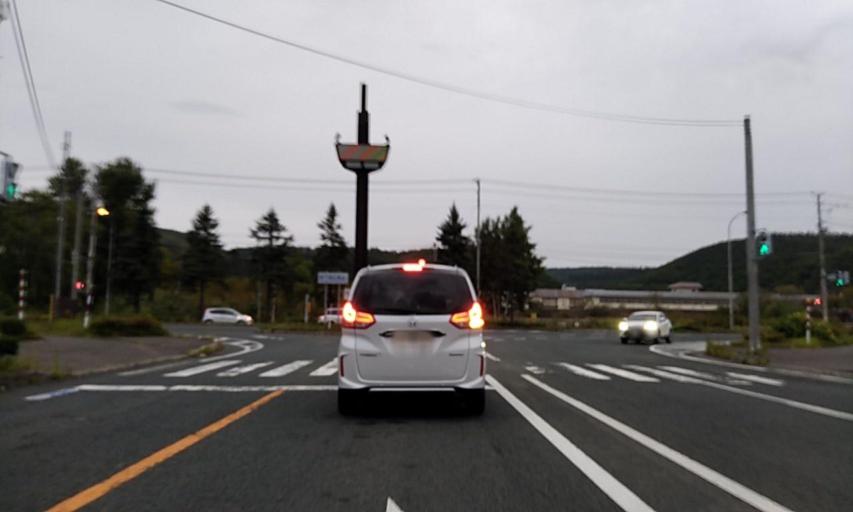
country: JP
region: Hokkaido
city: Abashiri
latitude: 44.0126
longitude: 144.2313
